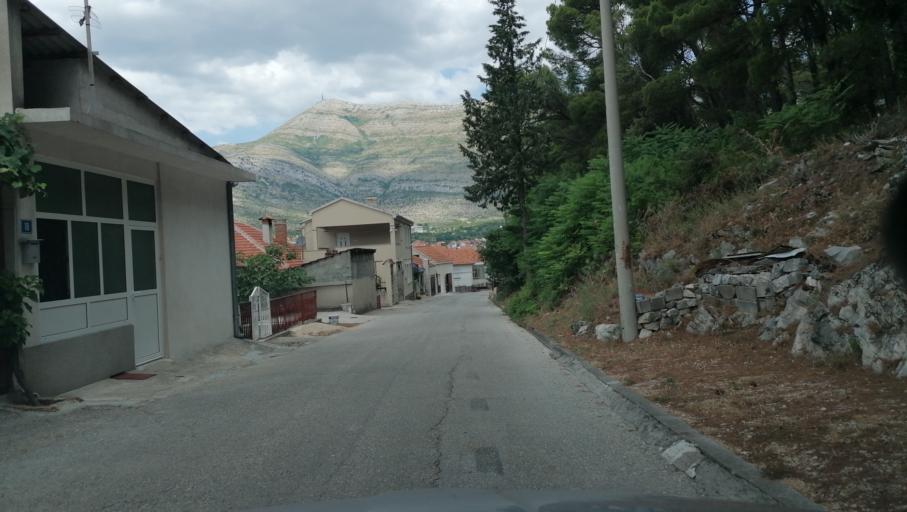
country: BA
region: Republika Srpska
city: Trebinje
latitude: 42.7109
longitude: 18.3571
